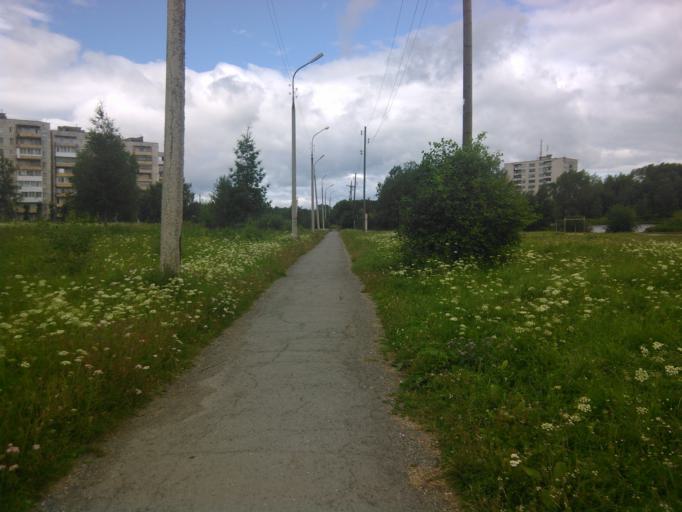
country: RU
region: Sverdlovsk
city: Krasnotur'insk
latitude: 59.7600
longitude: 60.1689
